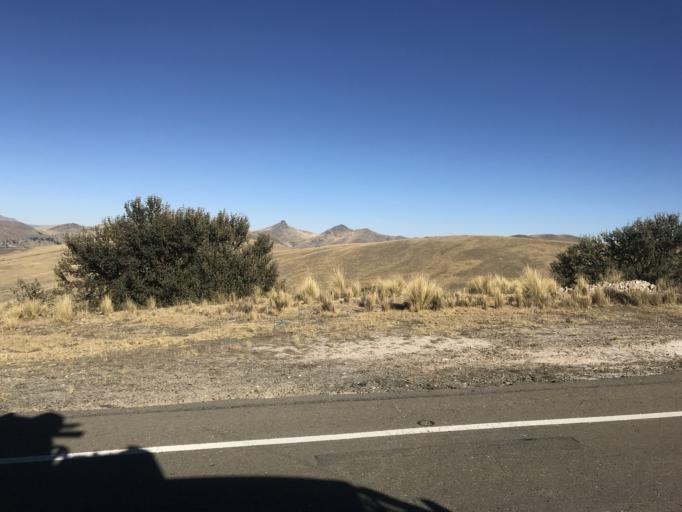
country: PE
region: Puno
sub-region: Yunguyo
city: Yunguyo
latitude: -16.1661
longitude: -68.9856
